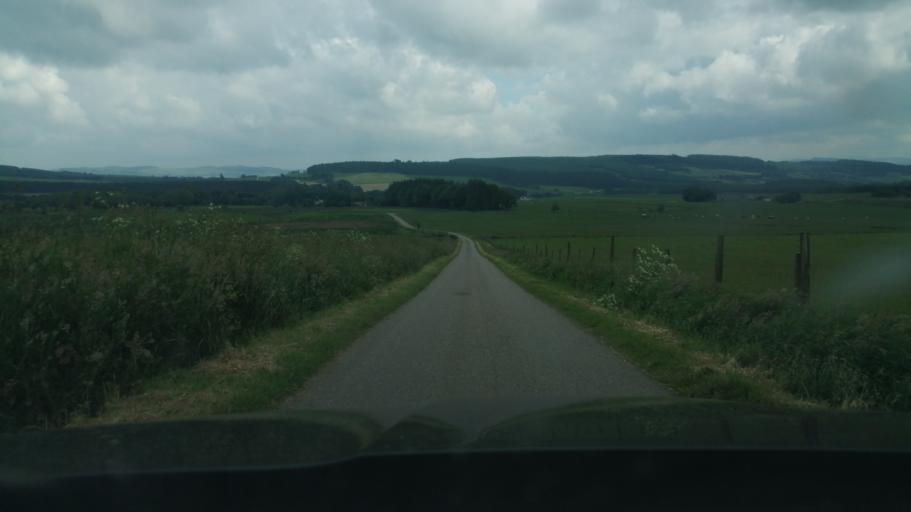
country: GB
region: Scotland
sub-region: Moray
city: Cullen
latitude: 57.5934
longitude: -2.8240
